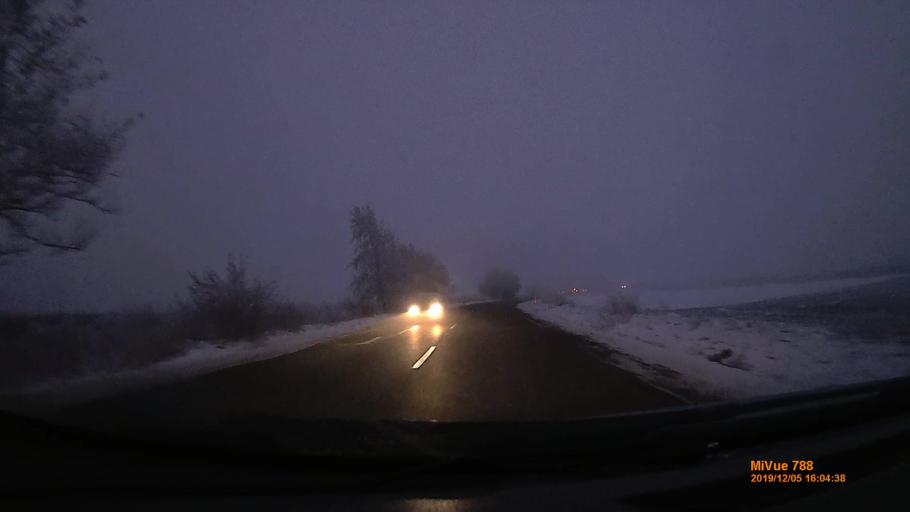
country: HU
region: Borsod-Abauj-Zemplen
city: Tarcal
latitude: 48.1095
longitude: 21.3530
